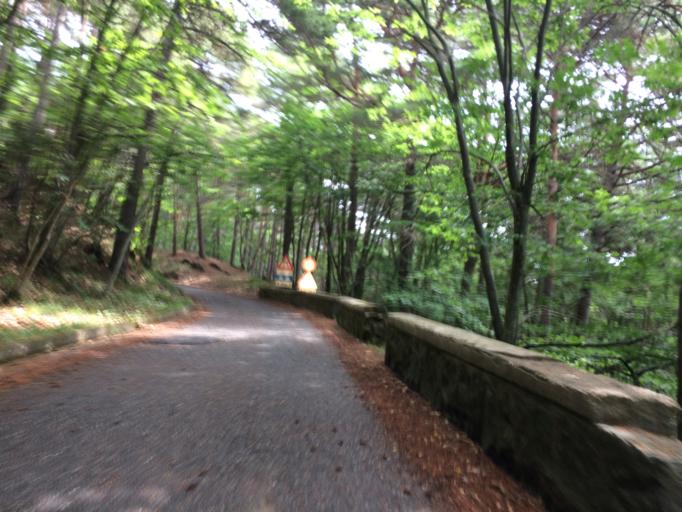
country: IT
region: Liguria
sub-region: Provincia di Imperia
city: Bajardo
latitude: 43.9011
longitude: 7.7285
